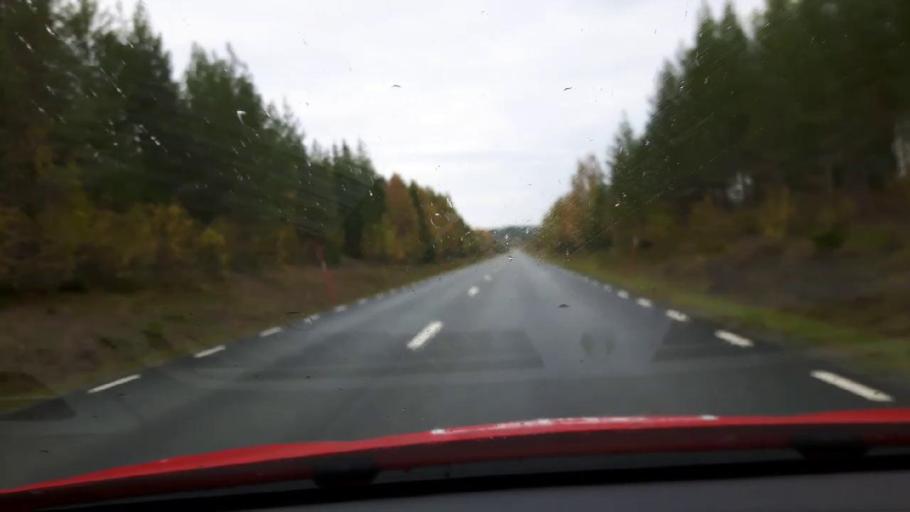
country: SE
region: Jaemtland
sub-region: Krokoms Kommun
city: Krokom
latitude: 63.0846
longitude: 14.2950
